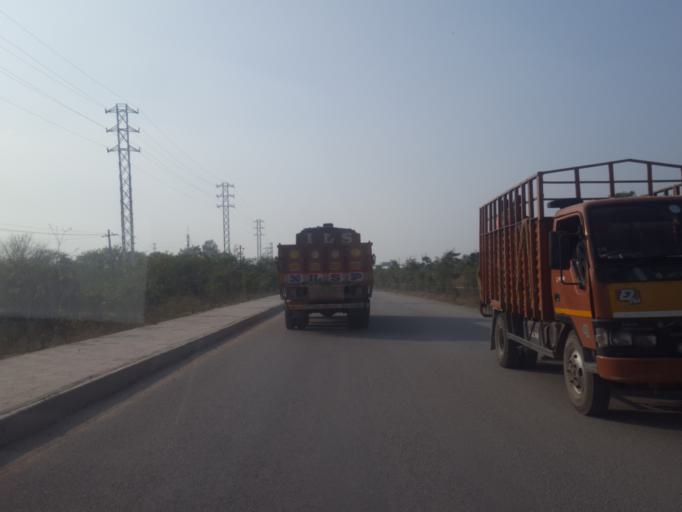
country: IN
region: Telangana
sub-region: Medak
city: Serilingampalle
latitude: 17.4108
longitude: 78.3174
